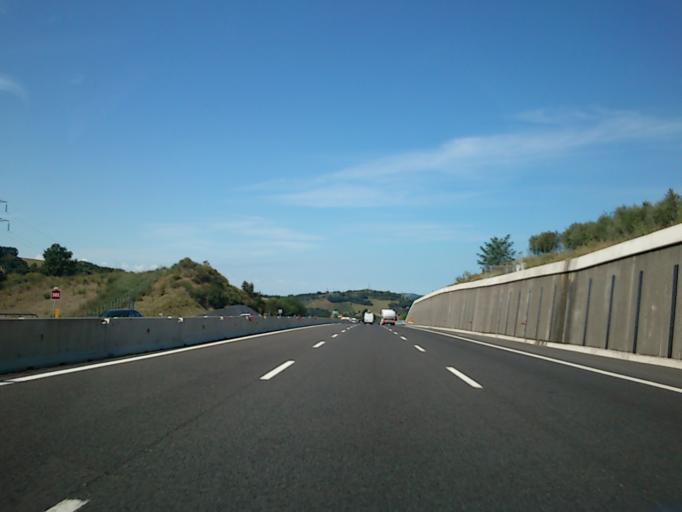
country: IT
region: The Marches
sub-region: Provincia di Pesaro e Urbino
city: Pesaro
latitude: 43.8707
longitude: 12.9213
